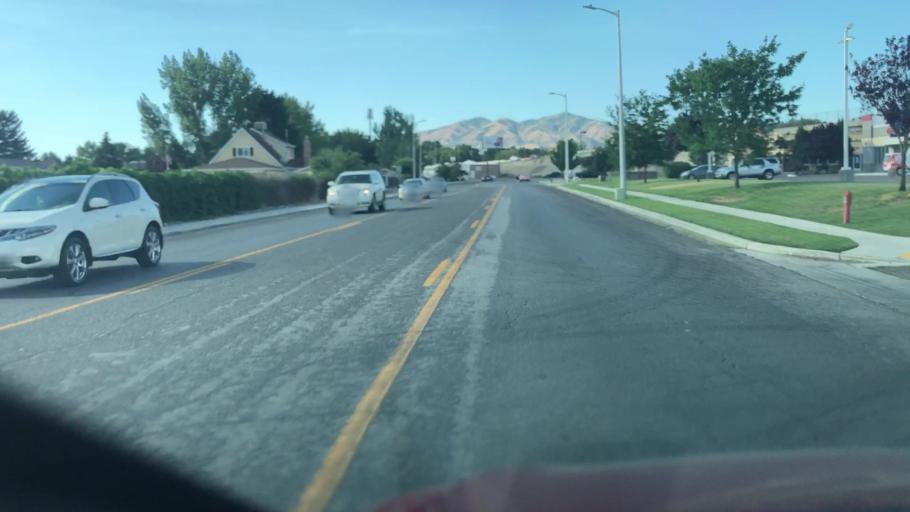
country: US
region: Utah
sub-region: Utah County
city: Lehi
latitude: 40.3910
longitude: -111.8366
